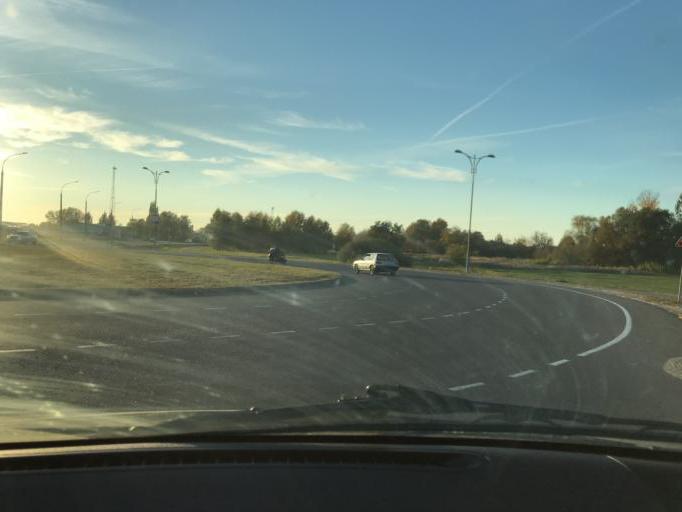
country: BY
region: Brest
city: Horad Kobryn
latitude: 52.2106
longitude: 24.3955
